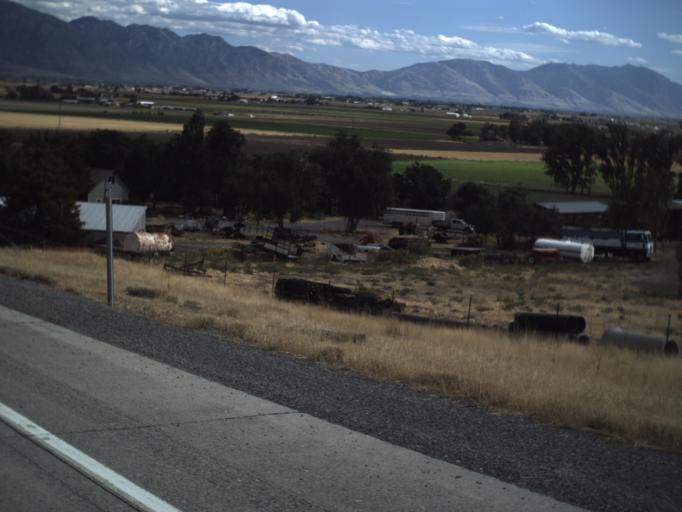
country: US
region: Utah
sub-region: Box Elder County
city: Tremonton
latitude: 41.7195
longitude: -112.2274
